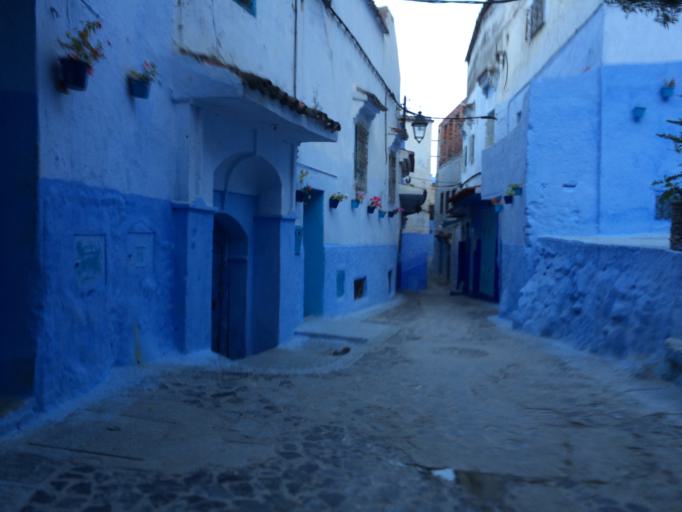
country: MA
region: Tanger-Tetouan
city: Chefchaouene
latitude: 35.1703
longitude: -5.2593
